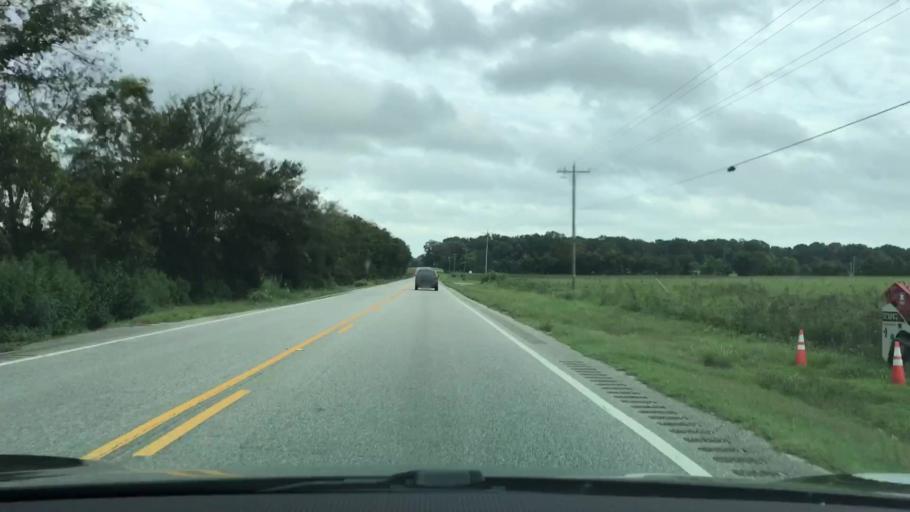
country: US
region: Alabama
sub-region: Montgomery County
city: Pike Road
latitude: 32.3214
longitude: -86.0490
